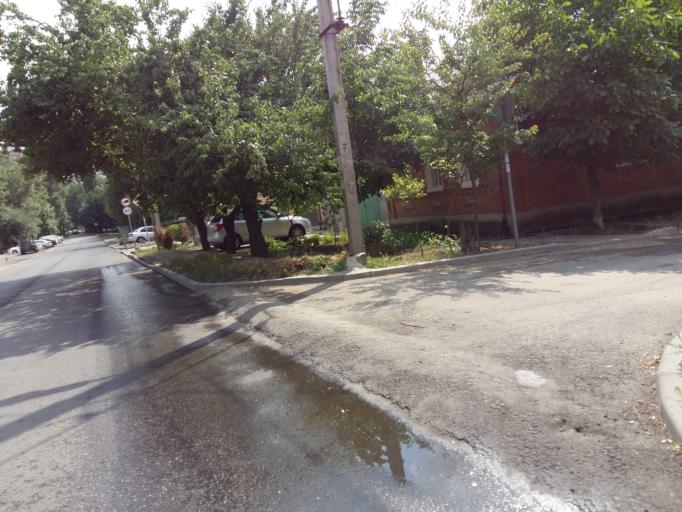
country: RU
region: Rostov
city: Imeni Chkalova
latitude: 47.2794
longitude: 39.7367
